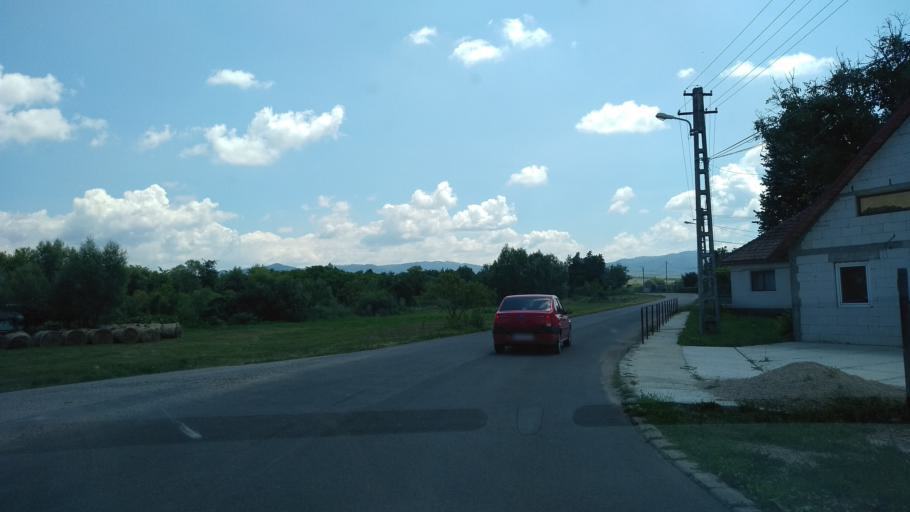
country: RO
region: Hunedoara
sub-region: Comuna Calan
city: Calan
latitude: 45.7188
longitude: 23.0348
